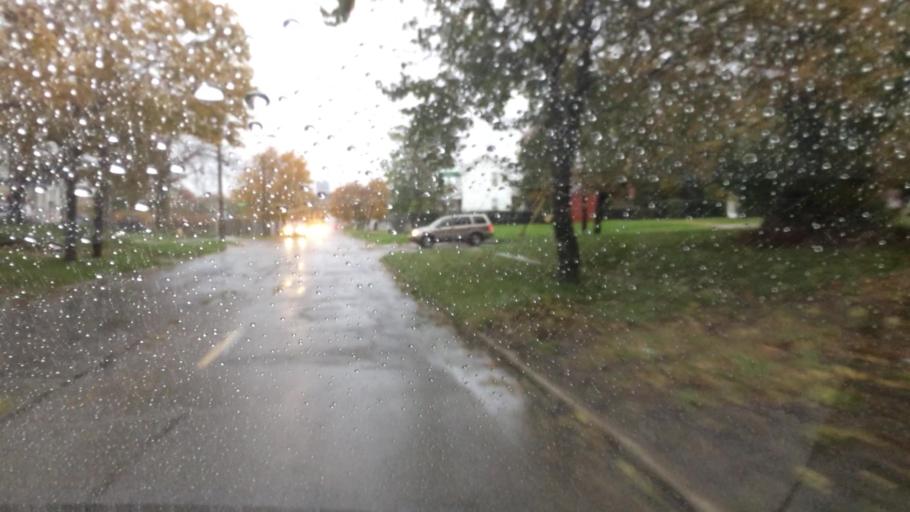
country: US
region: Ohio
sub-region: Summit County
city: Akron
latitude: 41.0559
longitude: -81.5195
